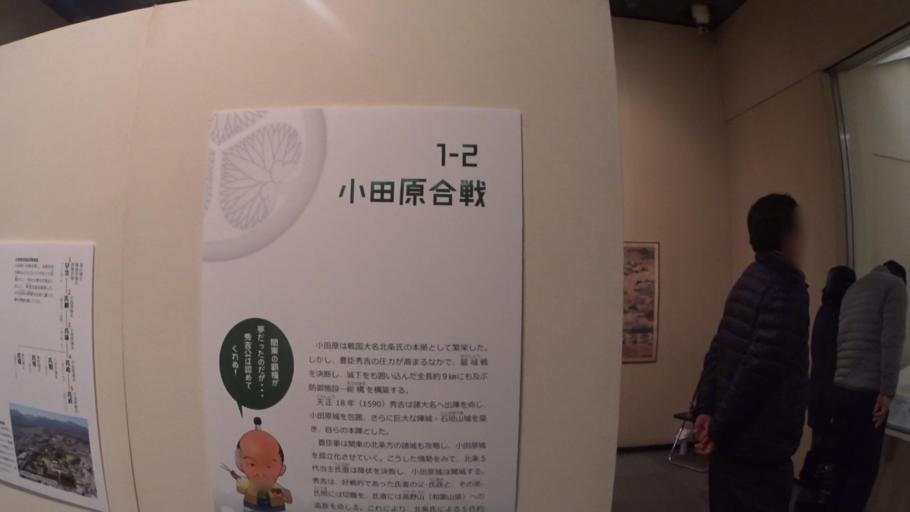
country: JP
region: Tokyo
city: Kokubunji
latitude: 35.6563
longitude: 139.4738
